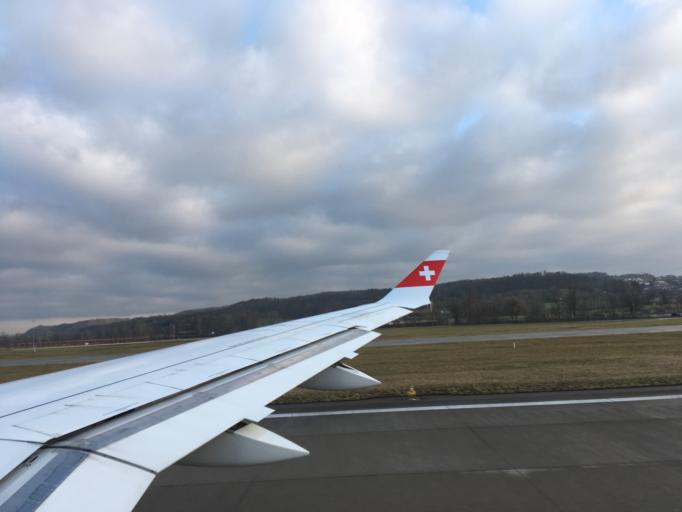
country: CH
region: Zurich
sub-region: Bezirk Buelach
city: Kloten / Holberg
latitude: 47.4568
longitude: 8.5684
